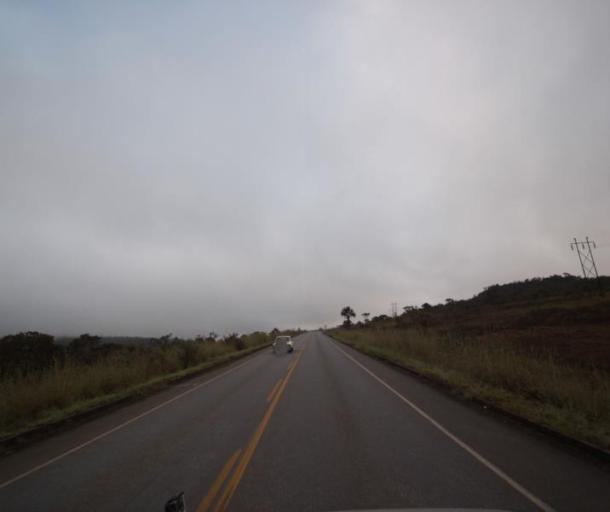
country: BR
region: Goias
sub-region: Pirenopolis
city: Pirenopolis
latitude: -15.8139
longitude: -48.7813
